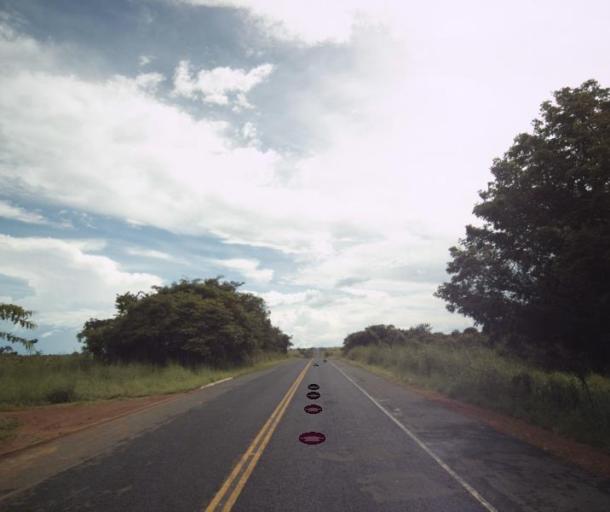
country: BR
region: Goias
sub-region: Sao Miguel Do Araguaia
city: Sao Miguel do Araguaia
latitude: -13.2888
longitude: -50.2032
